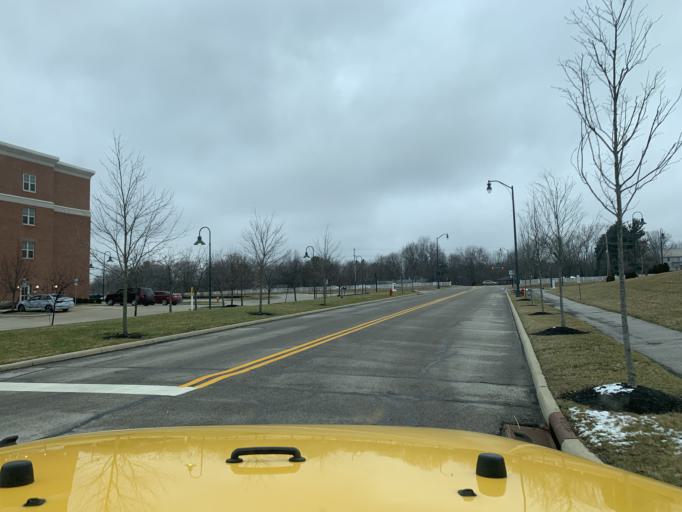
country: US
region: Ohio
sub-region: Franklin County
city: New Albany
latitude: 40.0913
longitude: -82.7874
